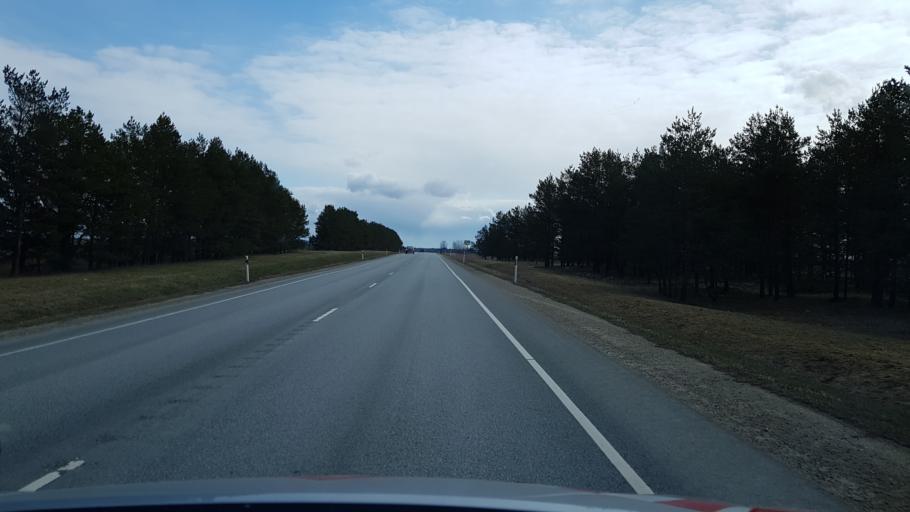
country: EE
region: Ida-Virumaa
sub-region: Puessi linn
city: Pussi
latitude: 59.4063
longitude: 27.0592
